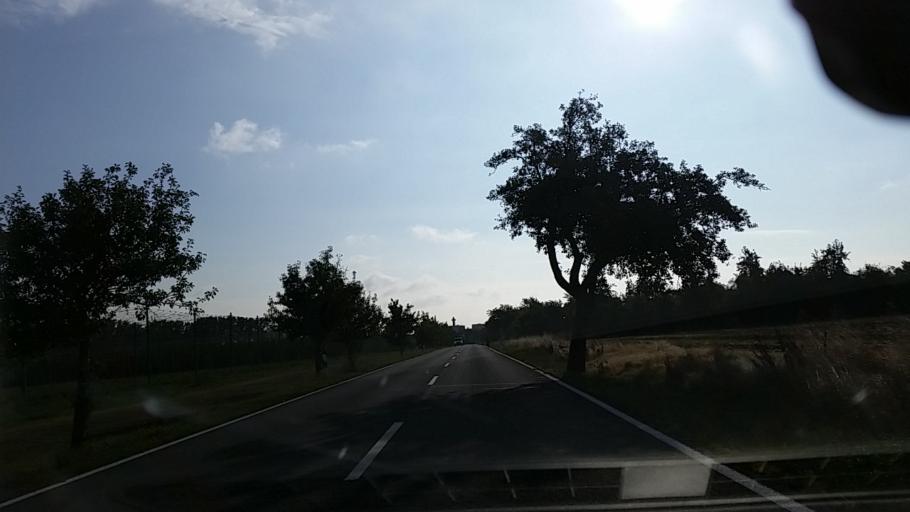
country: DE
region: Thuringia
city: Bad Frankenhausen
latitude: 51.3611
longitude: 11.0343
